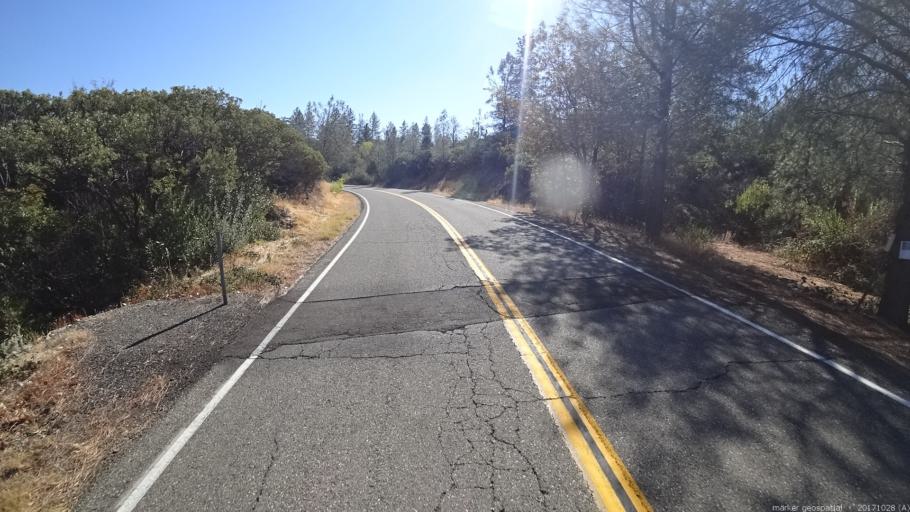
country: US
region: California
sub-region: Shasta County
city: Shasta
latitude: 40.6229
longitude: -122.4679
